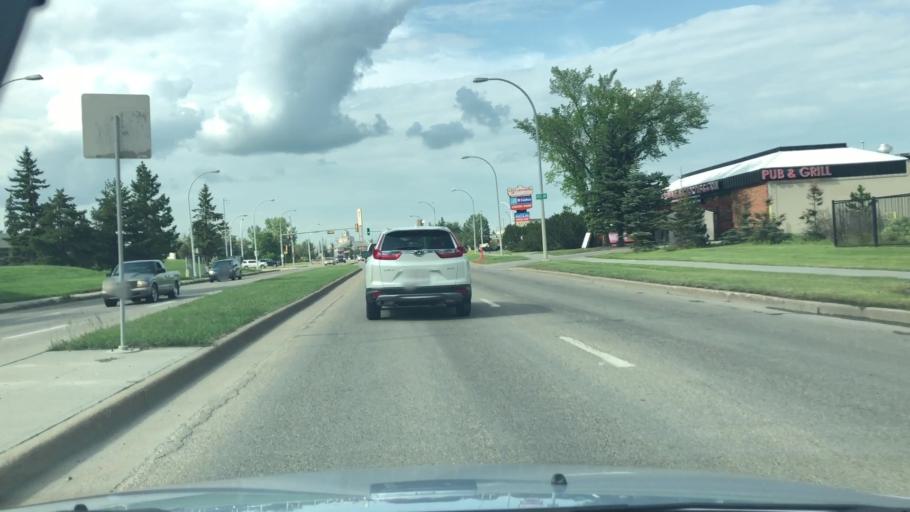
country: CA
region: Alberta
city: Edmonton
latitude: 53.6126
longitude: -113.5166
